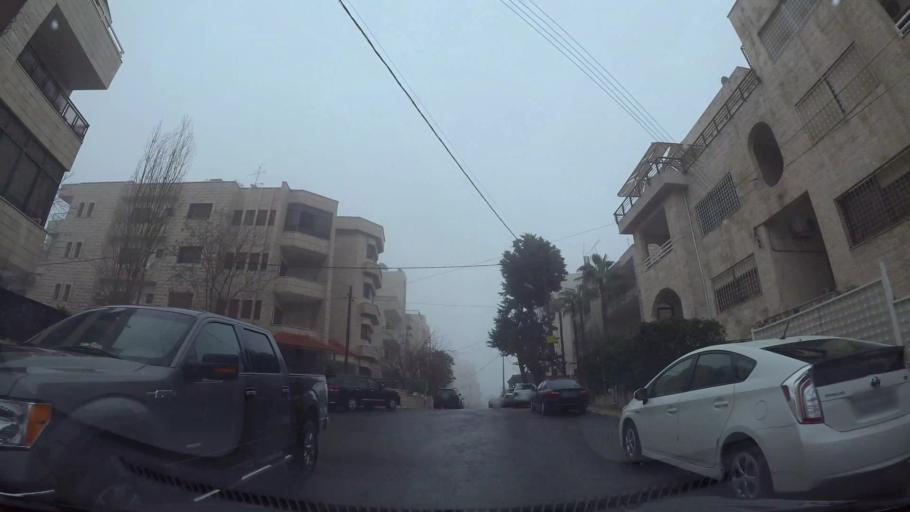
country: JO
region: Amman
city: Wadi as Sir
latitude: 31.9630
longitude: 35.8754
